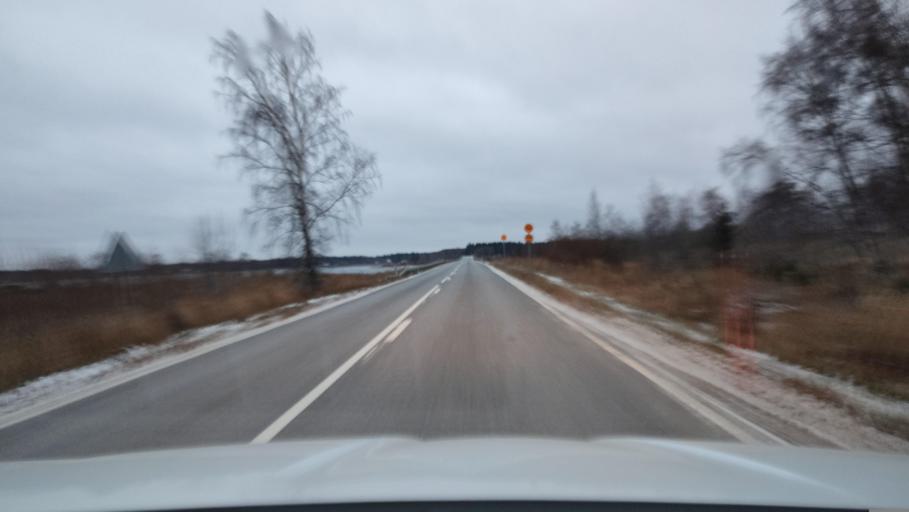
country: FI
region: Ostrobothnia
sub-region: Vaasa
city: Replot
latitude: 63.2788
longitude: 21.3416
